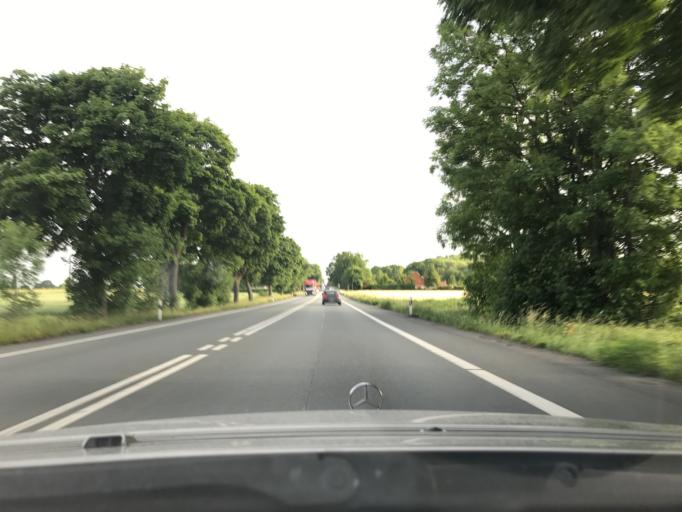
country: DE
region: North Rhine-Westphalia
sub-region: Regierungsbezirk Arnsberg
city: Werl
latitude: 51.6034
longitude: 7.8538
